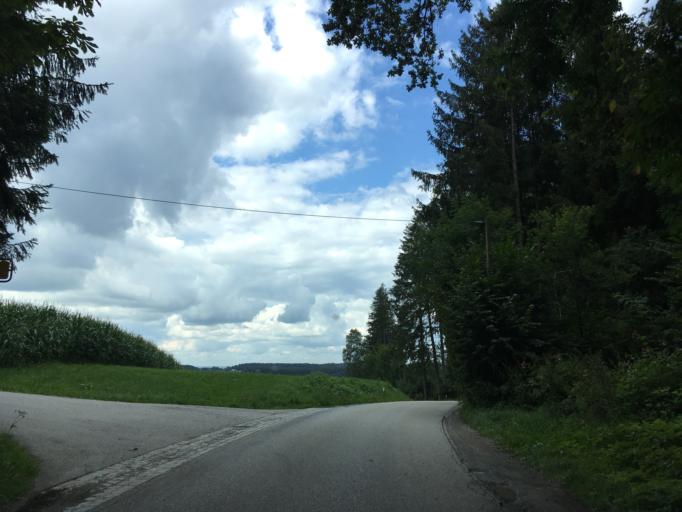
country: DE
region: Bavaria
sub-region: Upper Bavaria
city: Schnaitsee
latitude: 48.0474
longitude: 12.3437
